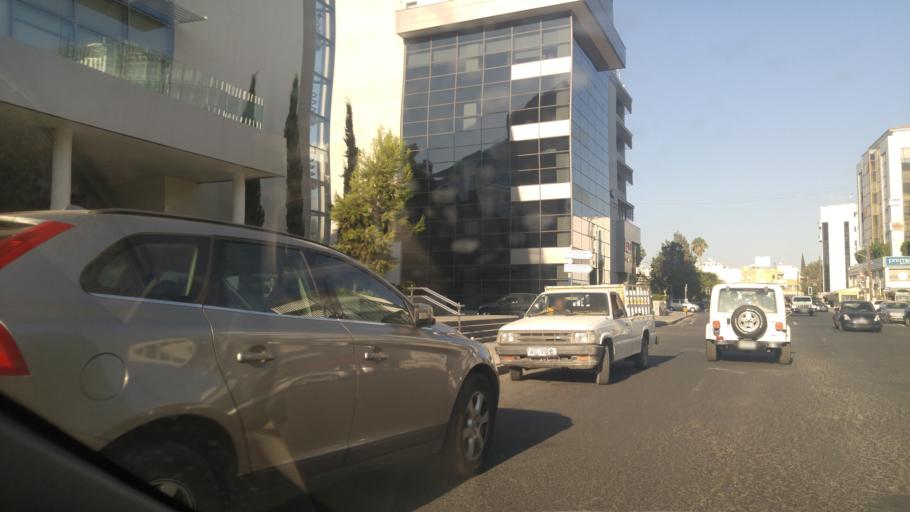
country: CY
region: Limassol
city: Limassol
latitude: 34.6826
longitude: 33.0471
